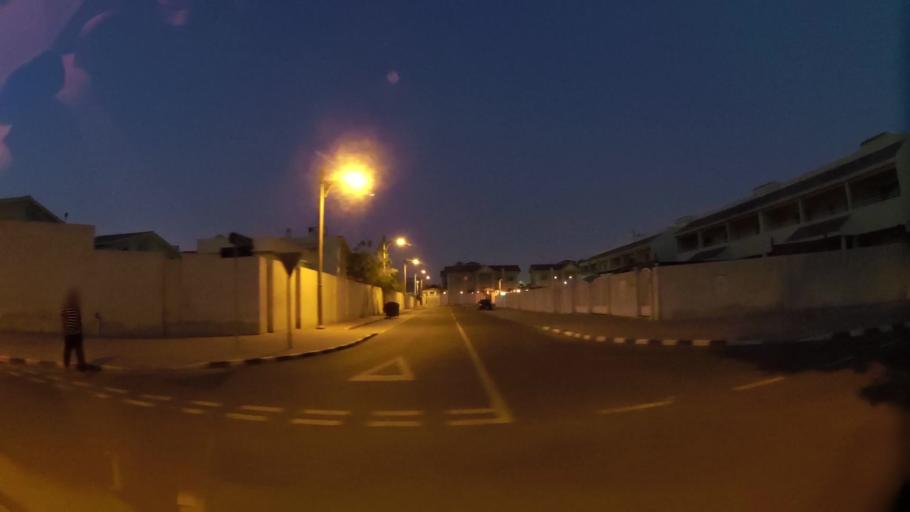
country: QA
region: Baladiyat ad Dawhah
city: Doha
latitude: 25.2577
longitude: 51.4812
